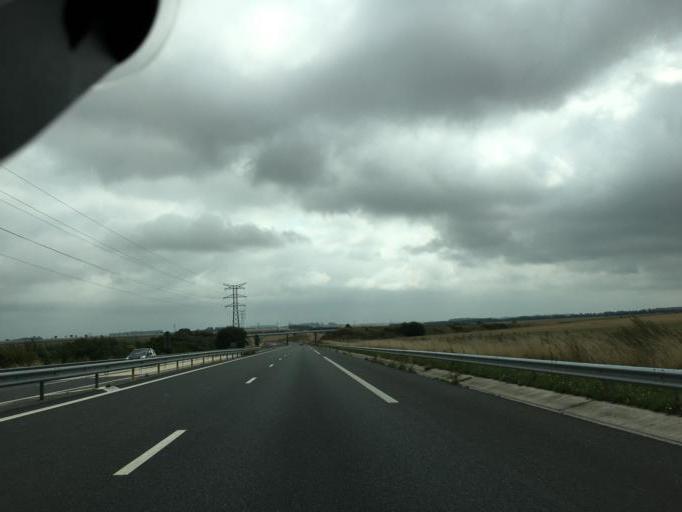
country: FR
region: Nord-Pas-de-Calais
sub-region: Departement du Pas-de-Calais
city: Montreuil
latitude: 50.4336
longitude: 1.7433
